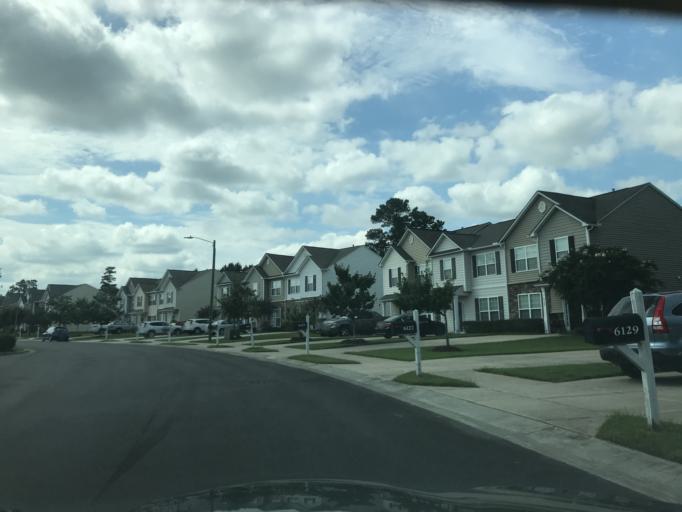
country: US
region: North Carolina
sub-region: Wake County
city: Rolesville
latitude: 35.8949
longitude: -78.5380
